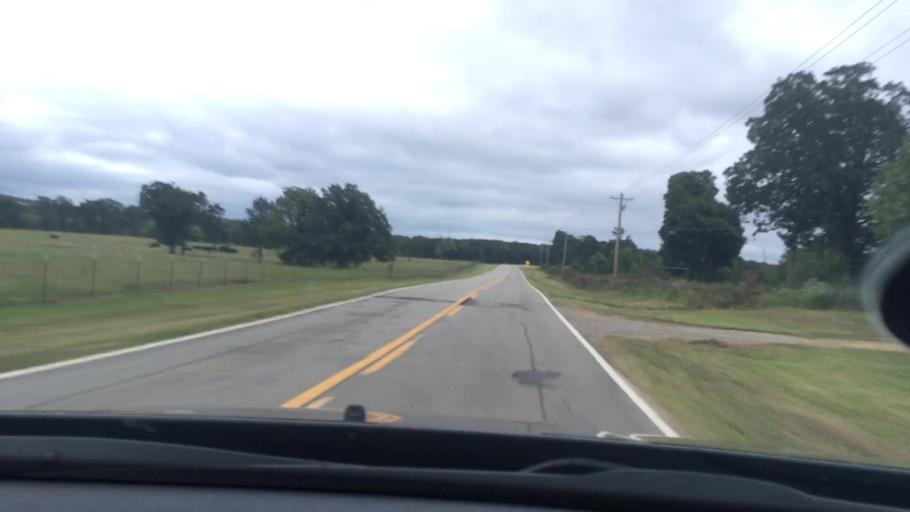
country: US
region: Oklahoma
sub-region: Sequoyah County
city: Vian
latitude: 35.6061
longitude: -95.0008
